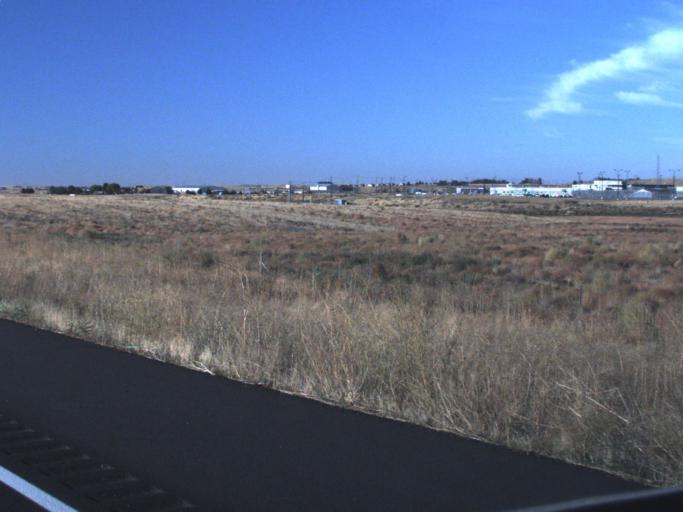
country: US
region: Washington
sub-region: Franklin County
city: Connell
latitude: 46.6811
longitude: -118.8426
